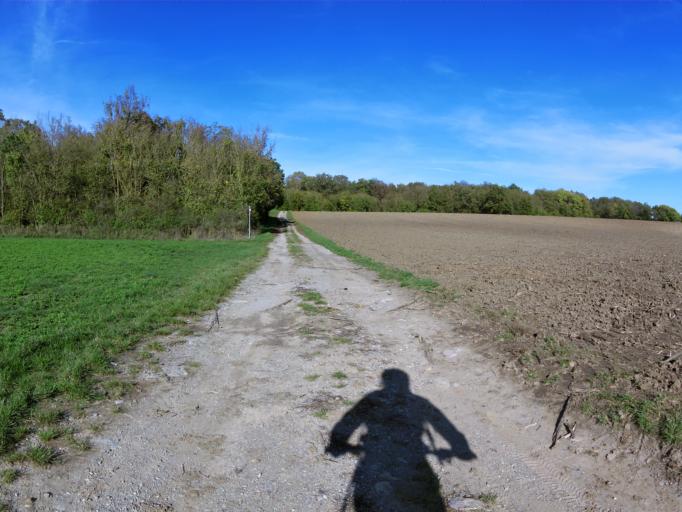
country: DE
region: Bavaria
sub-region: Regierungsbezirk Unterfranken
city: Frickenhausen
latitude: 49.7117
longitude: 10.0872
